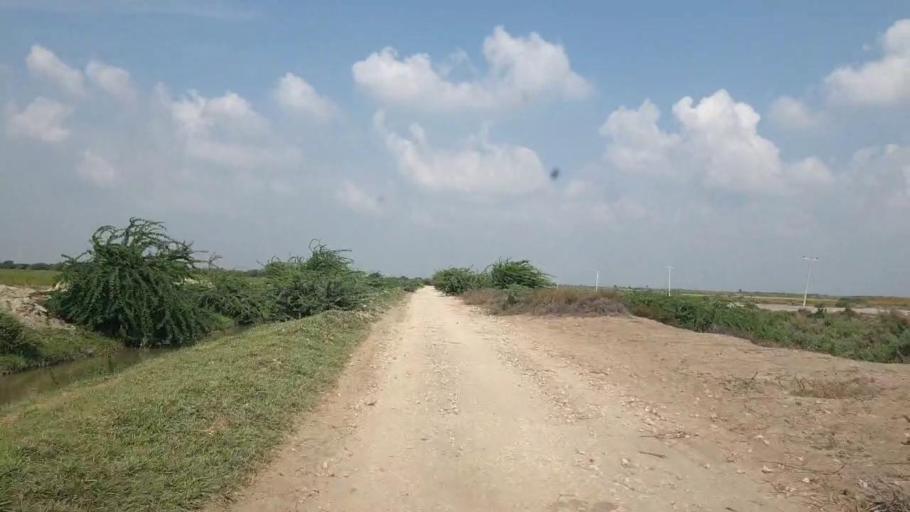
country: PK
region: Sindh
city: Badin
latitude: 24.4954
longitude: 68.6558
